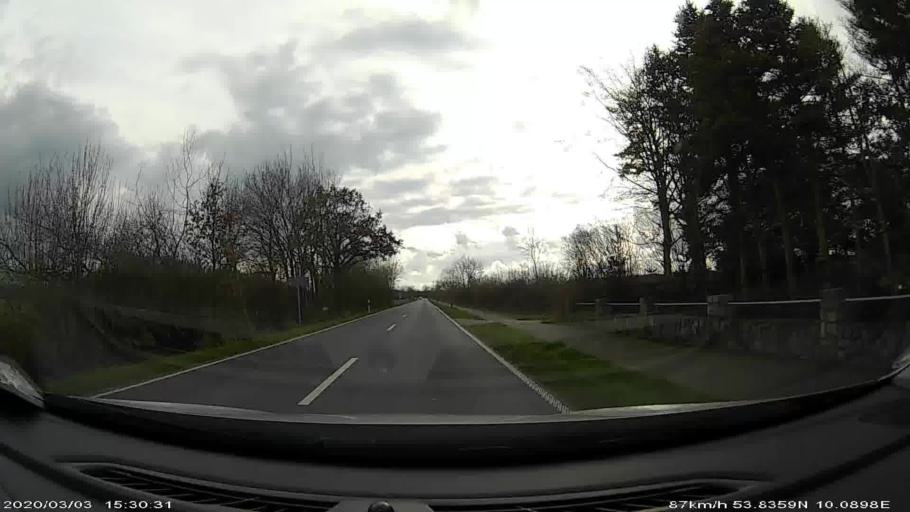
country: DE
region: Schleswig-Holstein
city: Sievershutten
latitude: 53.8370
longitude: 10.0909
